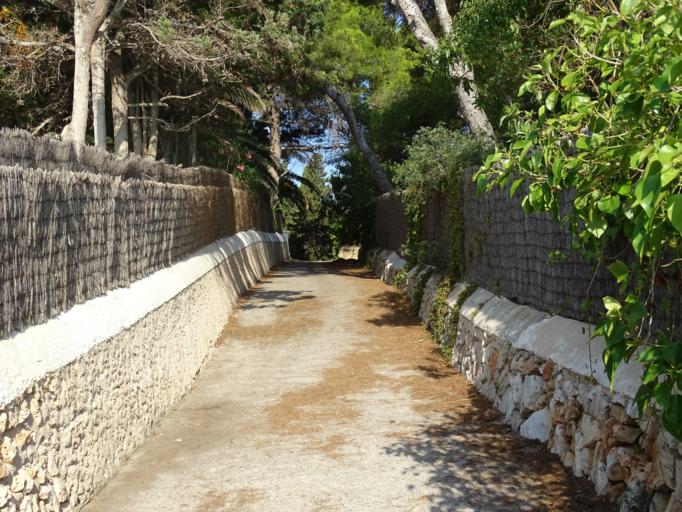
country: ES
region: Balearic Islands
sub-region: Illes Balears
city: Santanyi
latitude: 39.3686
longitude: 3.2312
